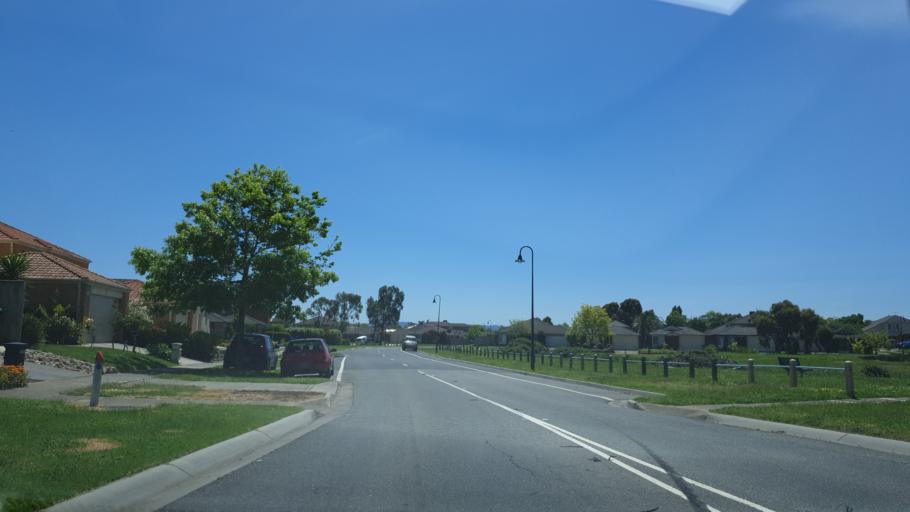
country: AU
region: Victoria
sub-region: Casey
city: Cranbourne North
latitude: -38.0675
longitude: 145.2826
